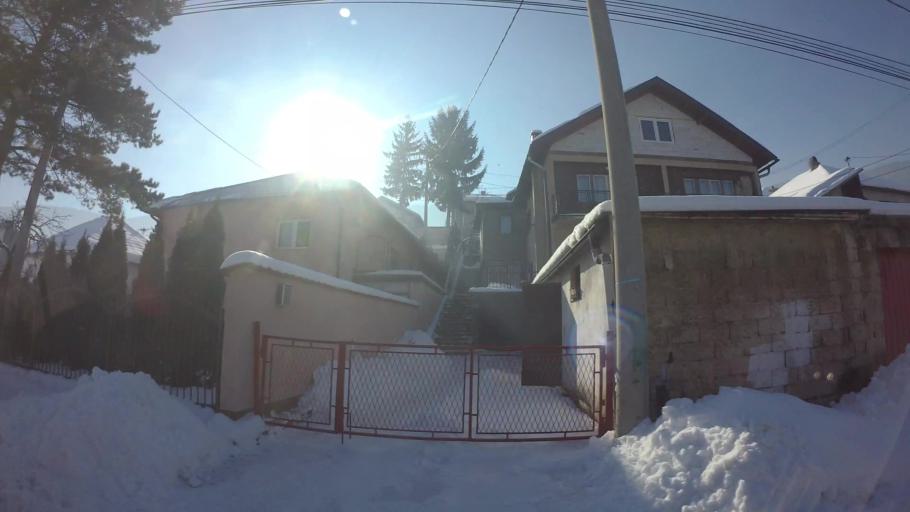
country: BA
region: Federation of Bosnia and Herzegovina
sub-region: Kanton Sarajevo
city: Sarajevo
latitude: 43.7942
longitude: 18.3197
